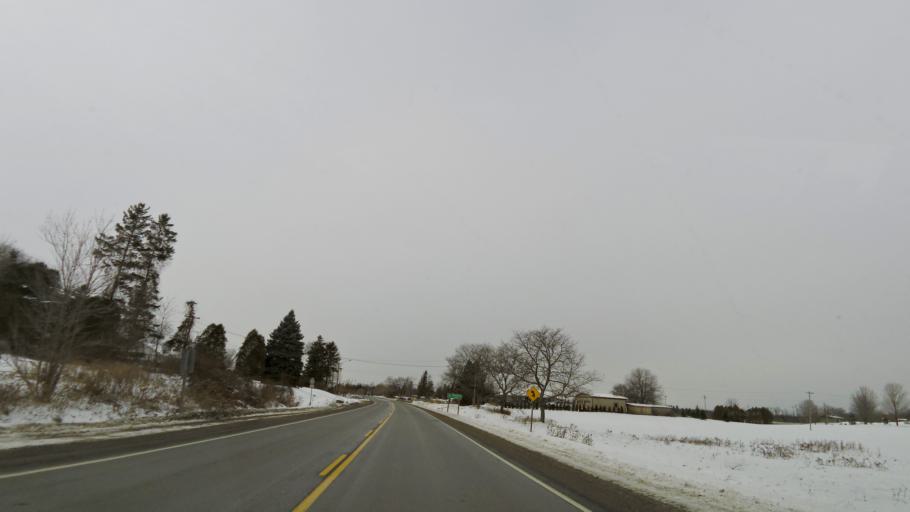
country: CA
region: Ontario
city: Ancaster
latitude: 43.2957
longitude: -80.1110
